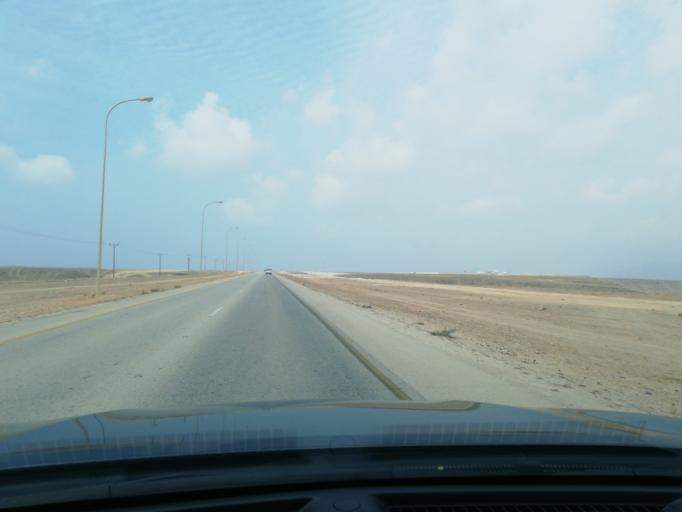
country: OM
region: Zufar
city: Salalah
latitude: 16.9477
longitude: 53.8527
